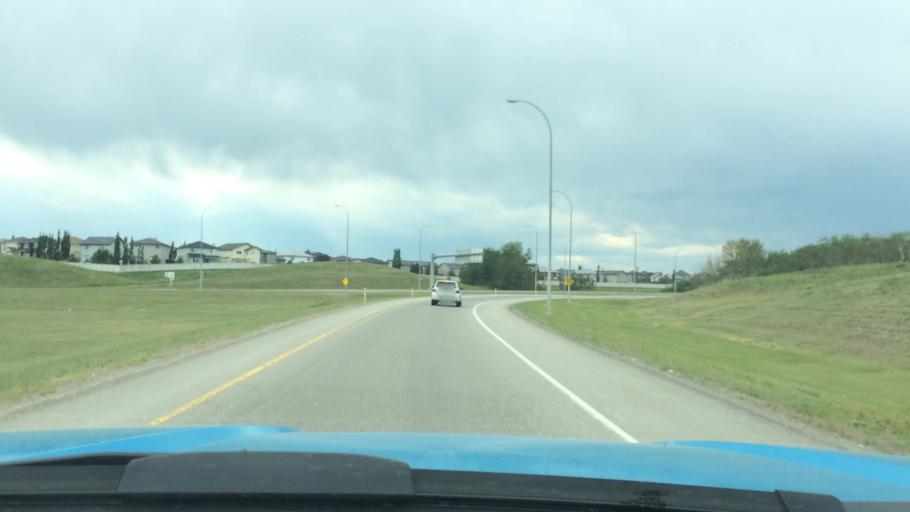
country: CA
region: Alberta
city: Calgary
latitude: 51.1466
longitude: -114.2057
